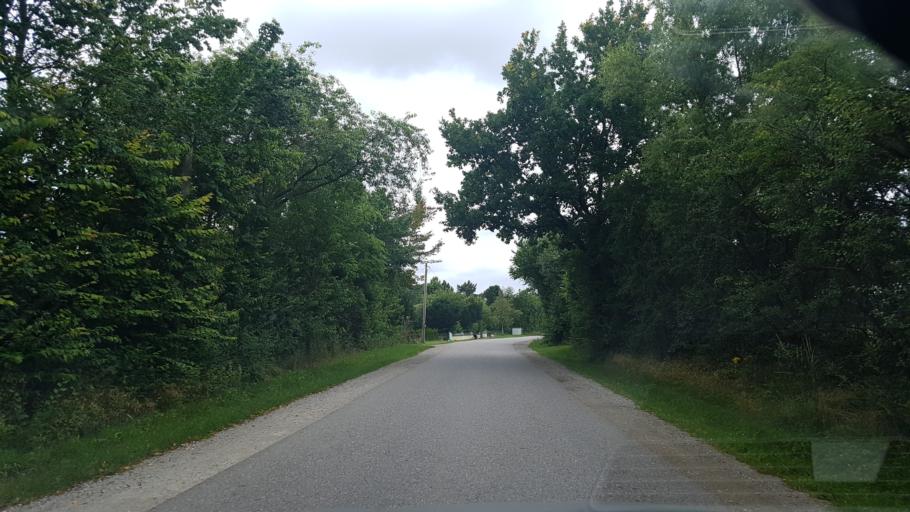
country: DE
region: Schleswig-Holstein
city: Osterby
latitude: 54.7930
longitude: 9.2390
